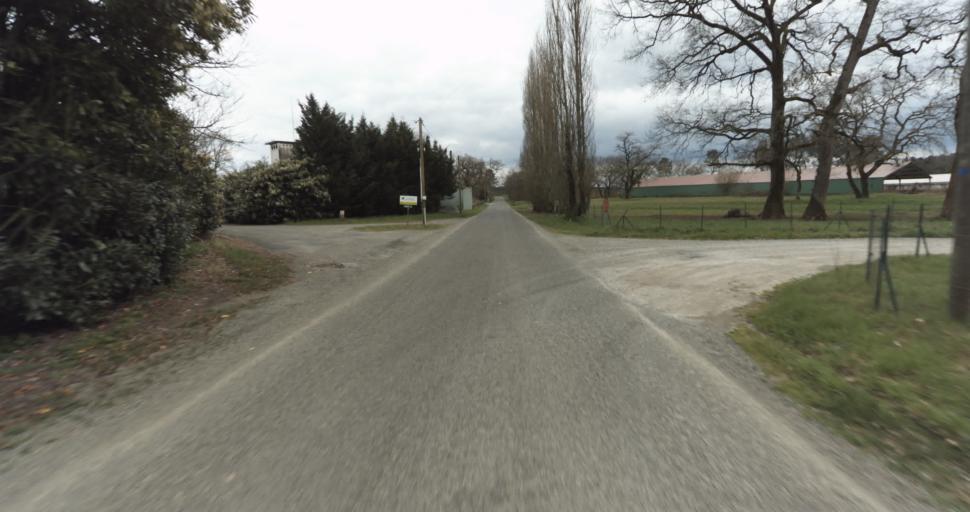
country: FR
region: Aquitaine
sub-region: Departement des Landes
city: Roquefort
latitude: 44.0155
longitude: -0.3410
